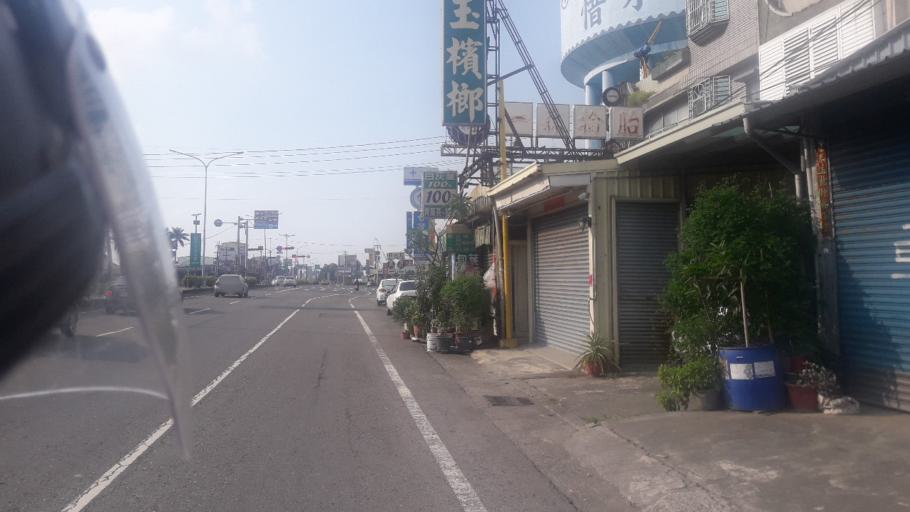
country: TW
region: Taiwan
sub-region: Tainan
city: Tainan
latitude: 22.8796
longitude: 120.2510
